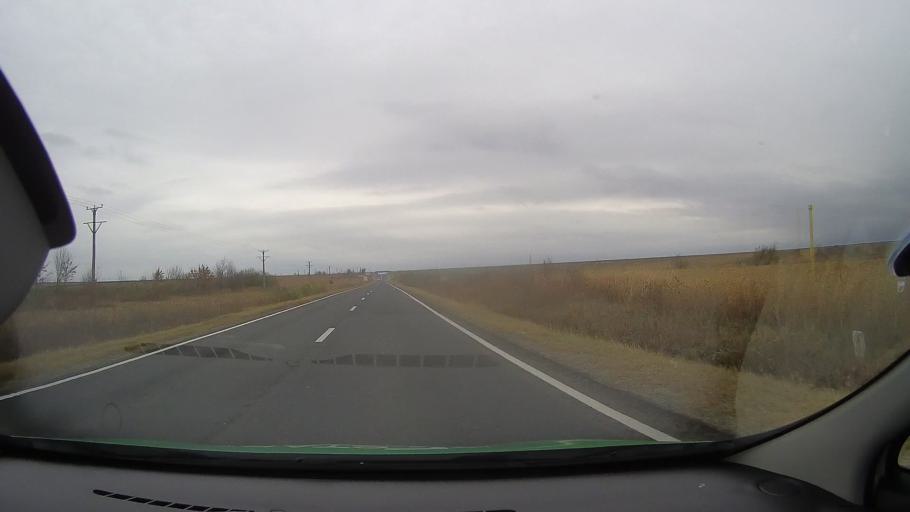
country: RO
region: Constanta
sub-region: Comuna Nicolae Balcescu
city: Nicolae Balcescu
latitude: 44.3845
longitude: 28.3952
